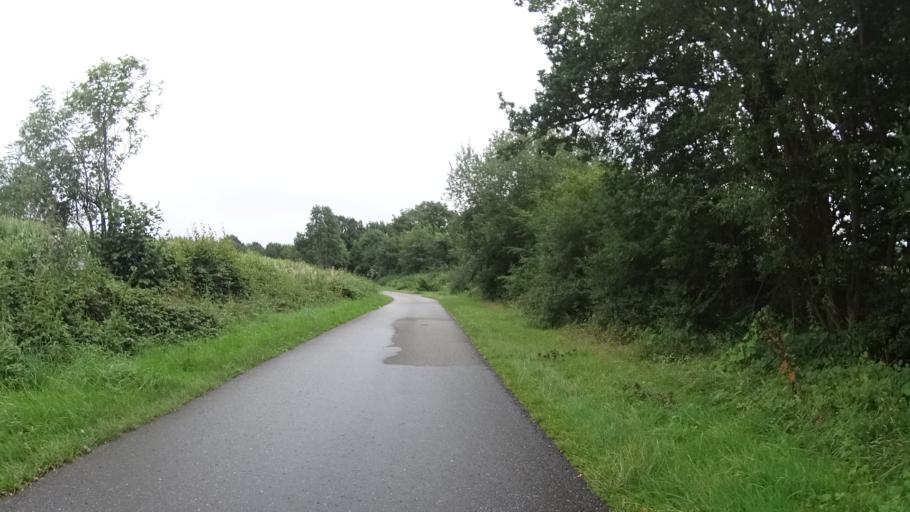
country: DE
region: Schleswig-Holstein
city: Stubben
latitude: 53.7140
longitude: 10.4450
